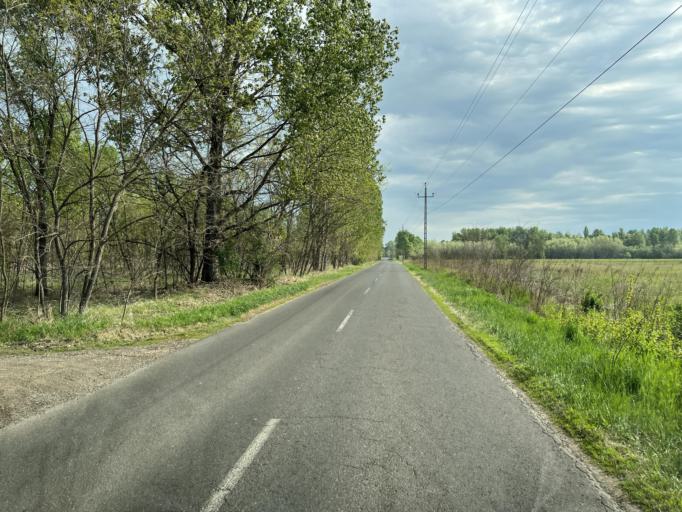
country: HU
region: Pest
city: Tapioszentmarton
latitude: 47.3508
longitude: 19.7874
